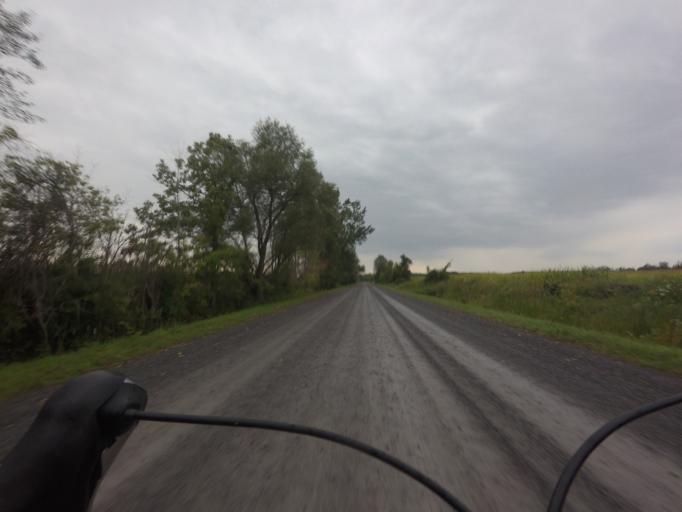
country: CA
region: Ontario
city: Bells Corners
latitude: 45.1675
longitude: -75.6827
